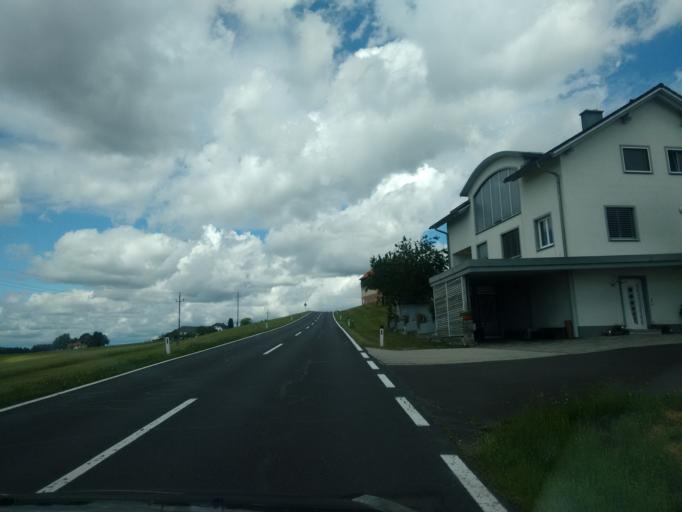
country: AT
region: Upper Austria
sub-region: Politischer Bezirk Urfahr-Umgebung
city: Gramastetten
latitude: 48.3943
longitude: 14.1831
